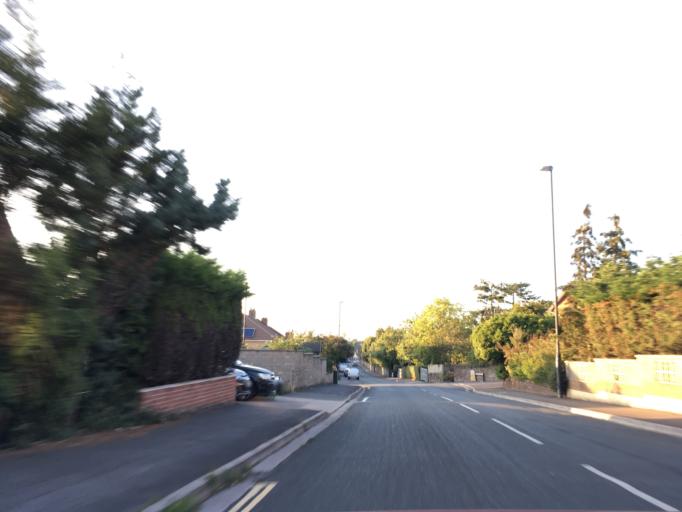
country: GB
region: England
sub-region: South Gloucestershire
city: Kingswood
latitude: 51.4441
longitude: -2.5409
